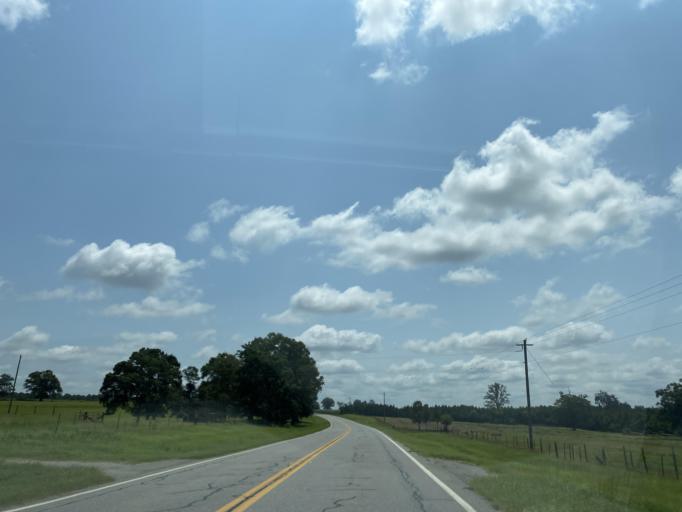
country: US
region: Georgia
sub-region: Wilcox County
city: Abbeville
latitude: 32.0030
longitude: -83.1515
